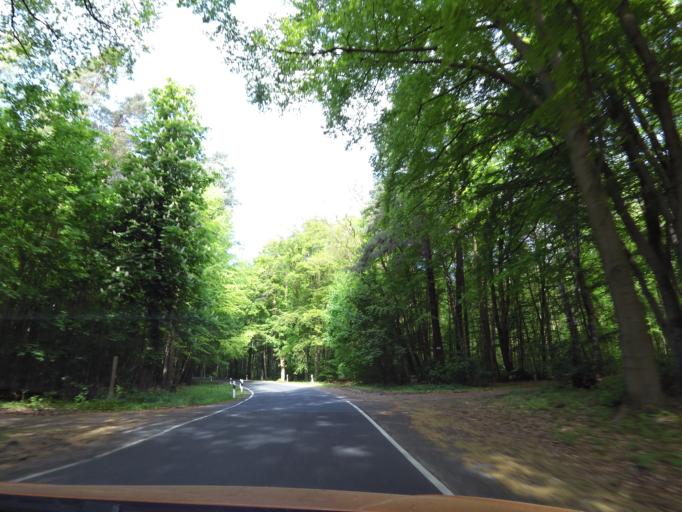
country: DE
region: Brandenburg
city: Wiesenburg
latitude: 52.0826
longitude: 12.5000
